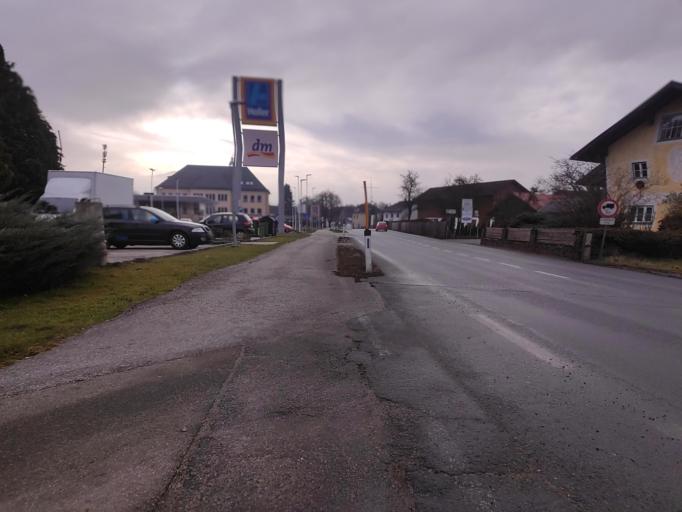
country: AT
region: Salzburg
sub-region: Politischer Bezirk Salzburg-Umgebung
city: Strasswalchen
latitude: 47.9838
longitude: 13.2539
